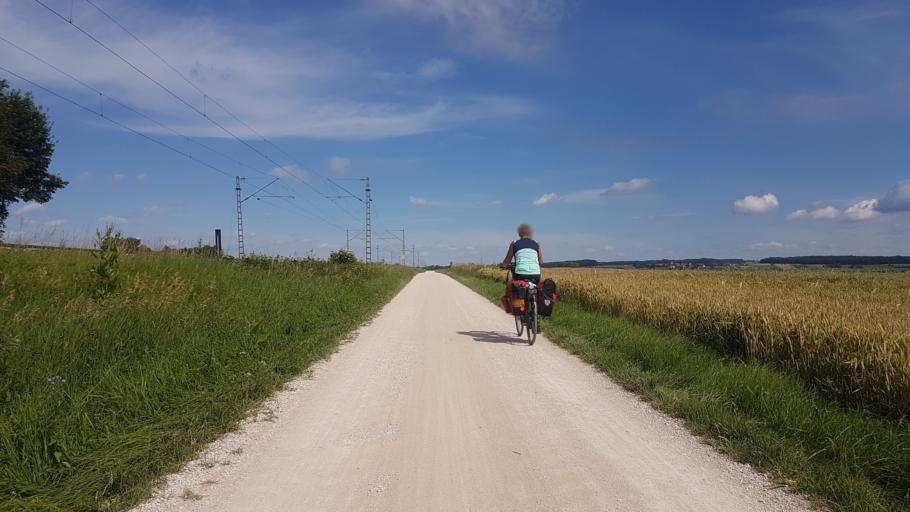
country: DE
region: Bavaria
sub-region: Regierungsbezirk Mittelfranken
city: Markt Berolzheim
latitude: 49.0257
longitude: 10.8466
